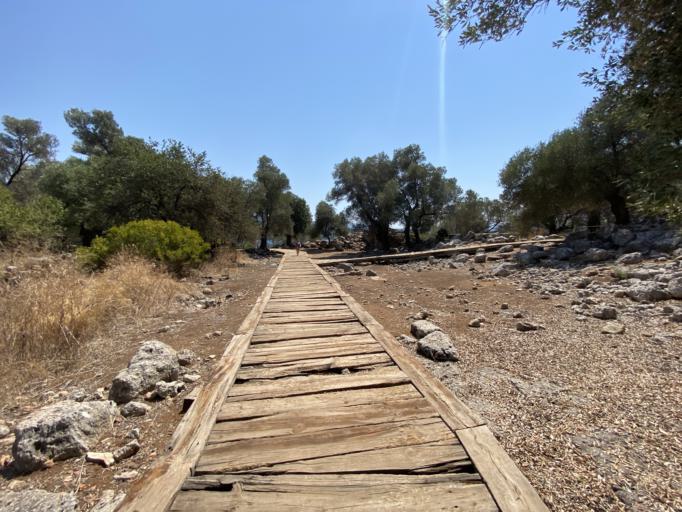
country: TR
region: Mugla
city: Yerkesik
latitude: 36.9920
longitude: 28.2069
